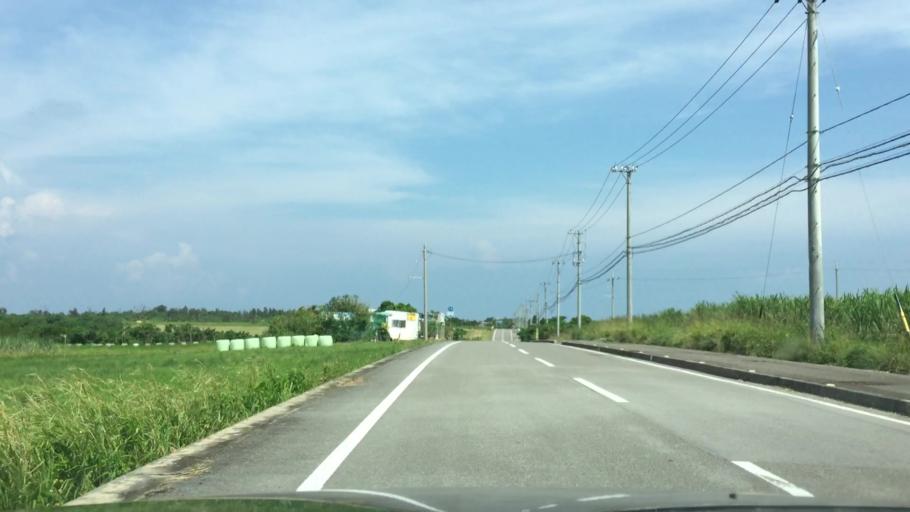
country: JP
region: Okinawa
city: Ishigaki
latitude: 24.5055
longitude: 124.2731
